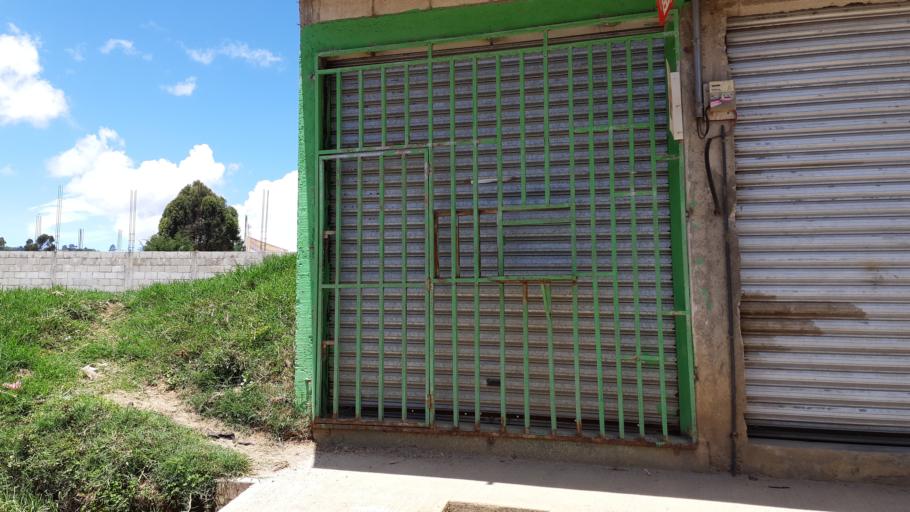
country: GT
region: Chimaltenango
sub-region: Municipio de Chimaltenango
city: Chimaltenango
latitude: 14.6642
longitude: -90.8454
